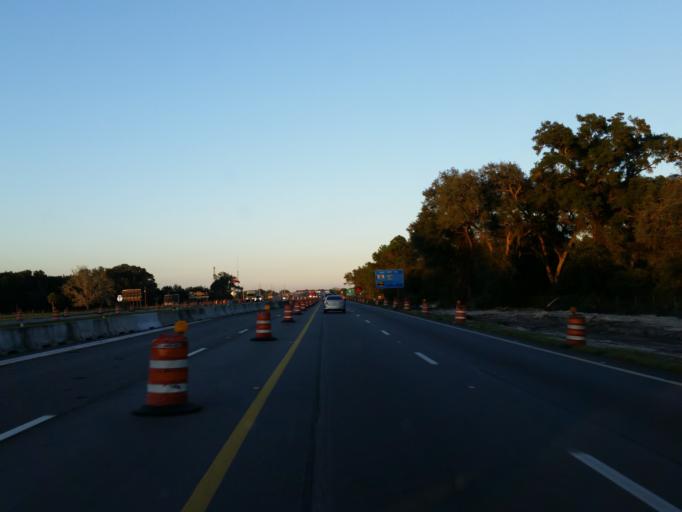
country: US
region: Florida
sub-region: Sumter County
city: Bushnell
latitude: 28.6614
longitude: -82.1476
